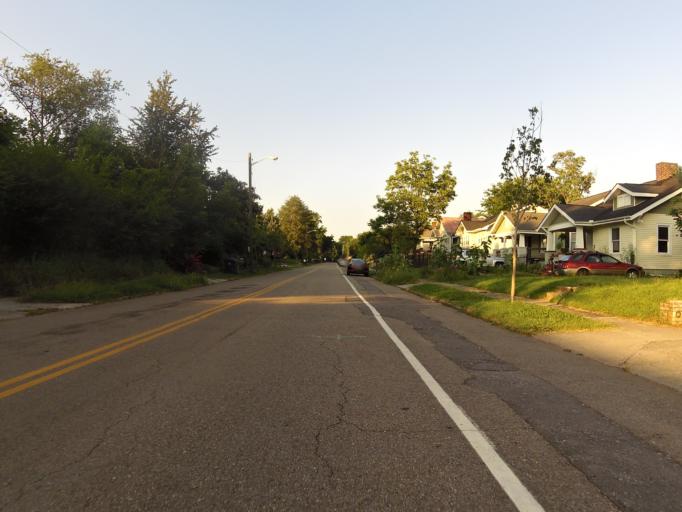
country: US
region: Tennessee
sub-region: Knox County
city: Knoxville
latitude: 35.9813
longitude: -83.9039
